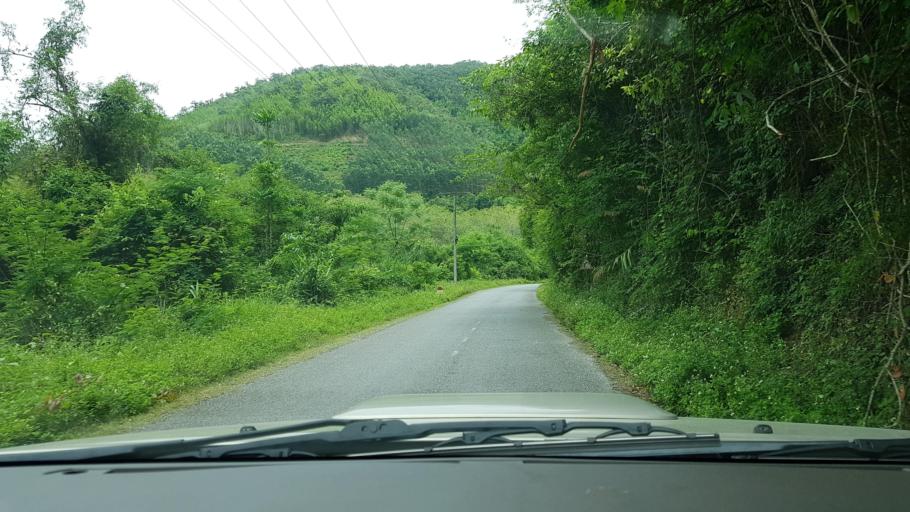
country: LA
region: Phongsali
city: Khoa
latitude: 21.0505
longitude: 102.4138
